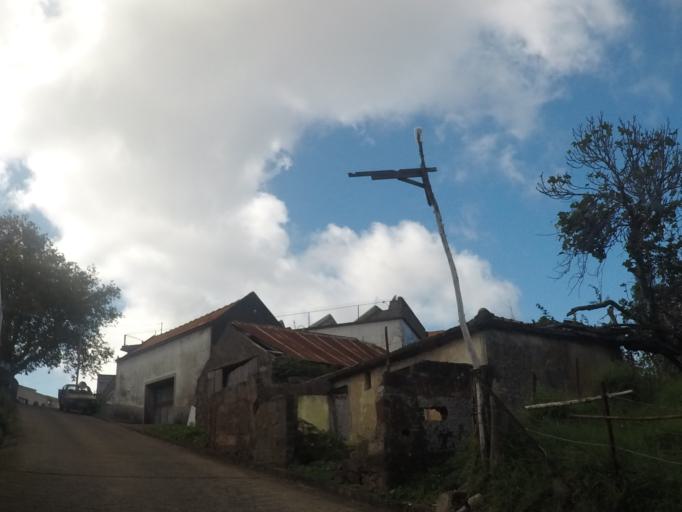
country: PT
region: Madeira
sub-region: Calheta
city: Faja da Ovelha
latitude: 32.8140
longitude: -17.2456
